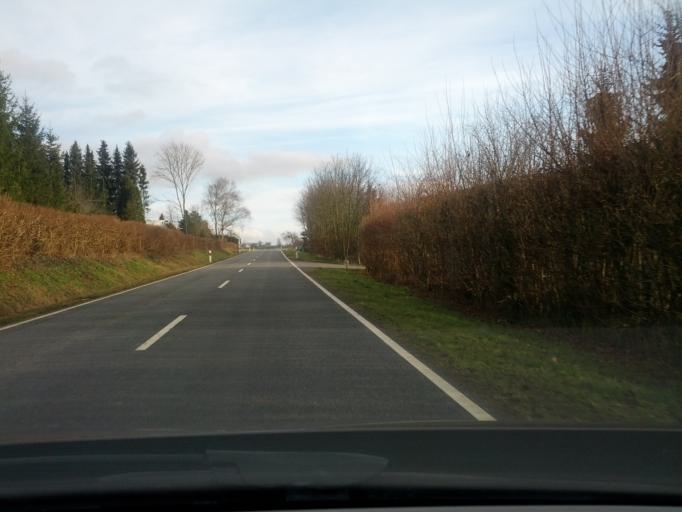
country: DE
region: Hesse
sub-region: Regierungsbezirk Kassel
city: Weissenborn
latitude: 51.0904
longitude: 10.1081
